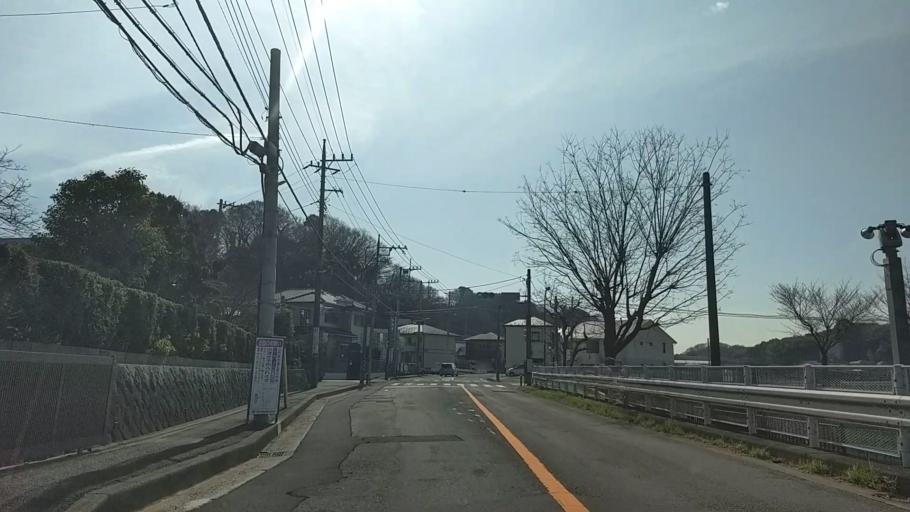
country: JP
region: Kanagawa
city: Kamakura
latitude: 35.4074
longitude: 139.5519
